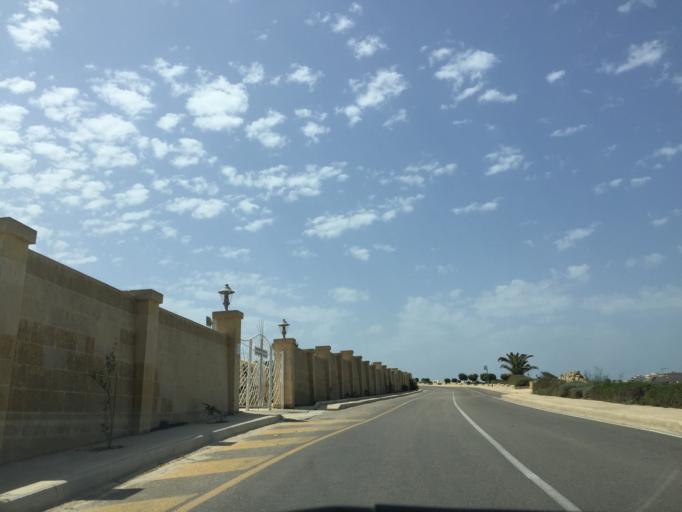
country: MT
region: In-Nadur
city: Nadur
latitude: 36.0530
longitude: 14.2914
